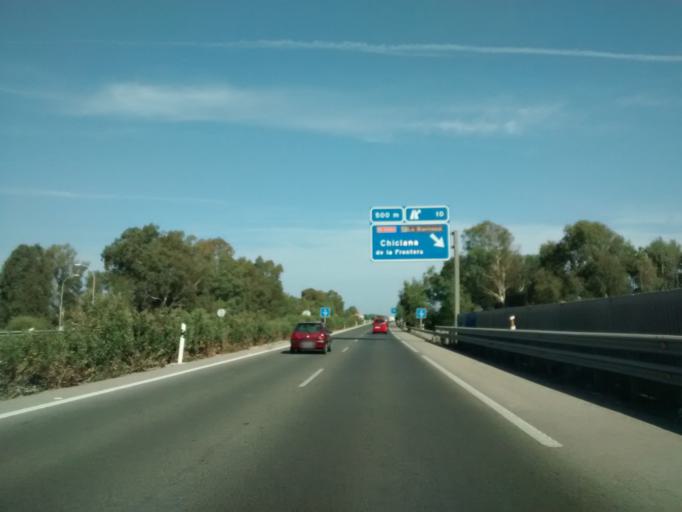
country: ES
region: Andalusia
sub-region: Provincia de Cadiz
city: Chiclana de la Frontera
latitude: 36.3916
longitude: -6.1205
